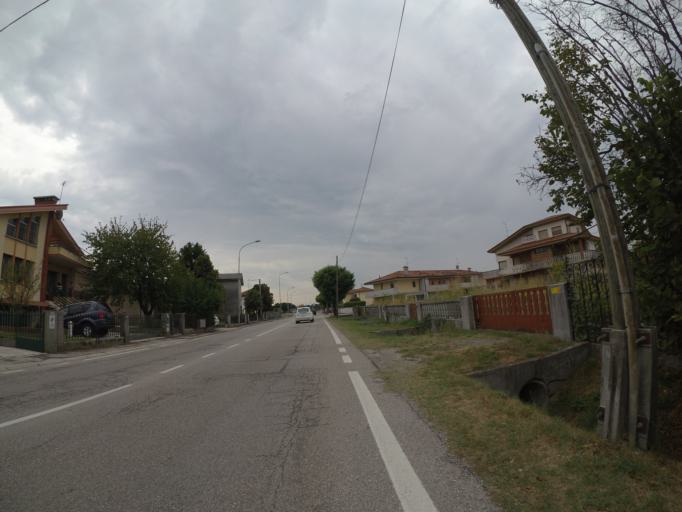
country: IT
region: Friuli Venezia Giulia
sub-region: Provincia di Udine
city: Codroipo
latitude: 45.9532
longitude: 12.9729
